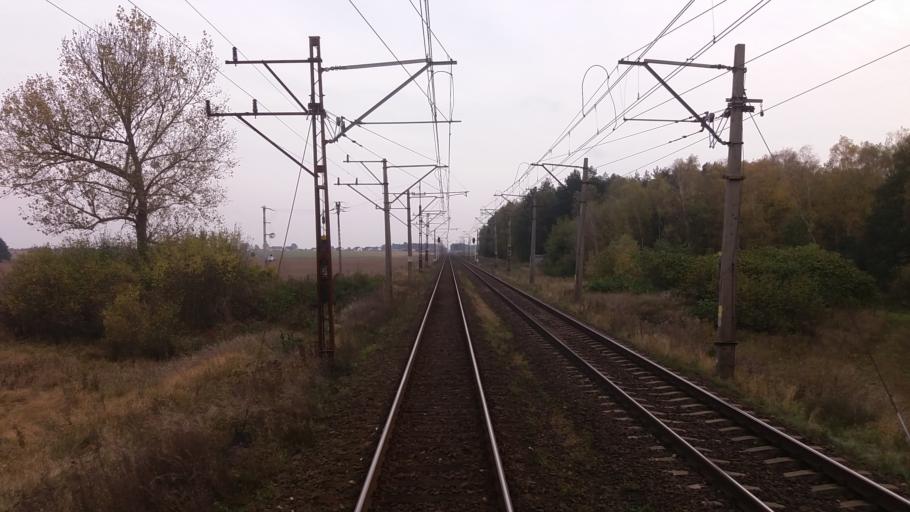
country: PL
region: West Pomeranian Voivodeship
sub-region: Powiat stargardzki
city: Kobylanka
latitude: 53.3619
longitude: 14.9458
